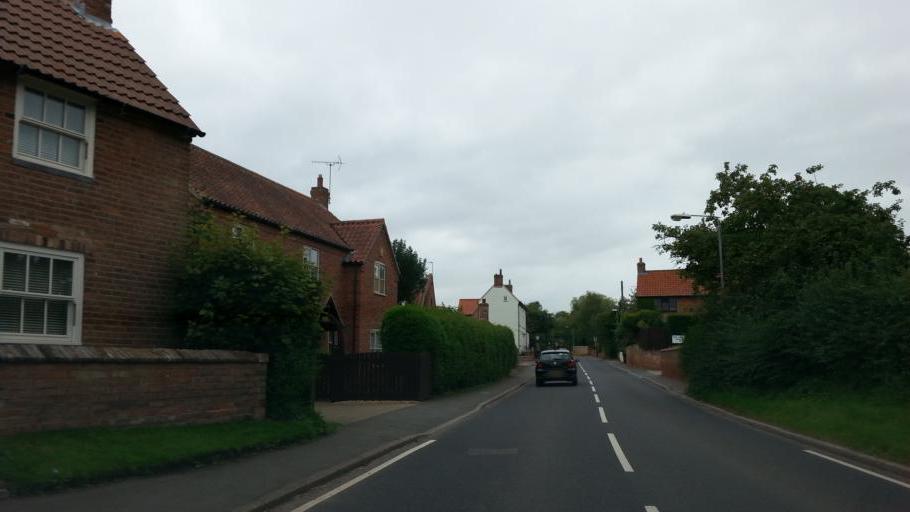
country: GB
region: England
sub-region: Nottinghamshire
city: Southwell
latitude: 53.0818
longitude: -0.8983
